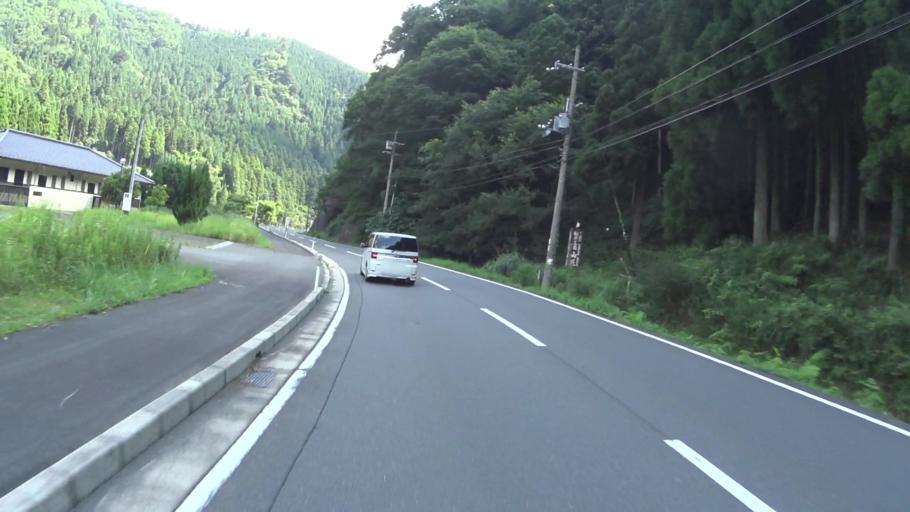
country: JP
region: Kyoto
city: Maizuru
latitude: 35.3156
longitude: 135.5559
